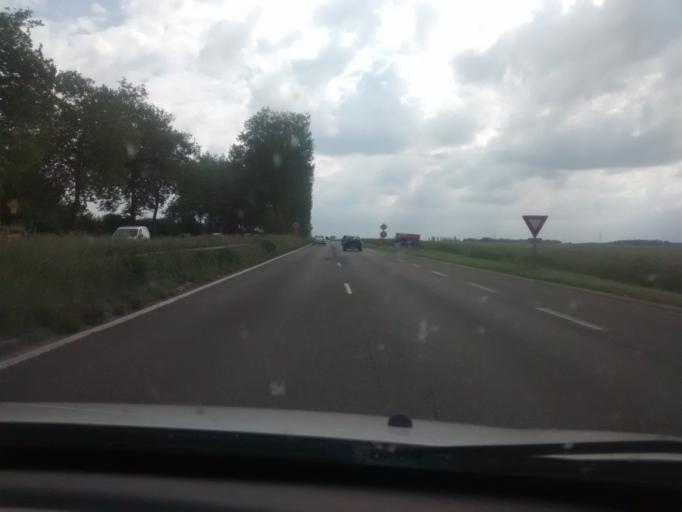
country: FR
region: Ile-de-France
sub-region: Departement des Yvelines
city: Coignieres
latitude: 48.7364
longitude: 1.9062
